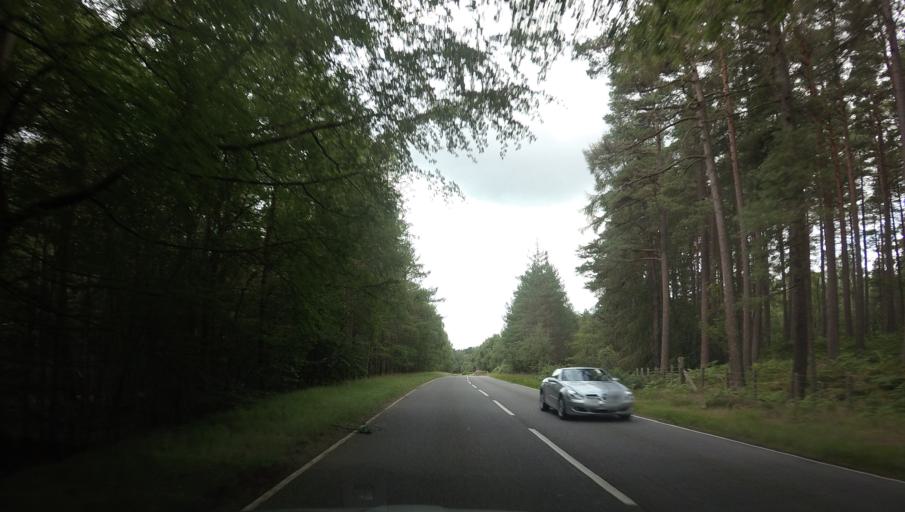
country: GB
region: Scotland
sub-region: Aberdeenshire
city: Torphins
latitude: 57.0610
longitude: -2.6107
